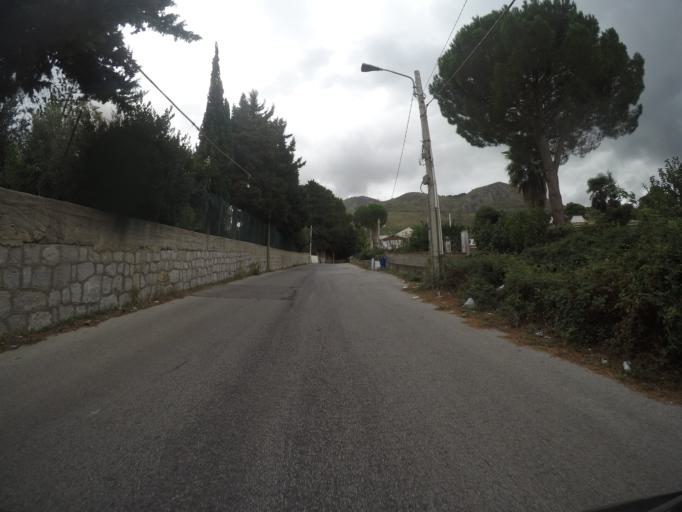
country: IT
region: Sicily
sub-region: Palermo
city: Carini
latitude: 38.1272
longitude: 13.1819
